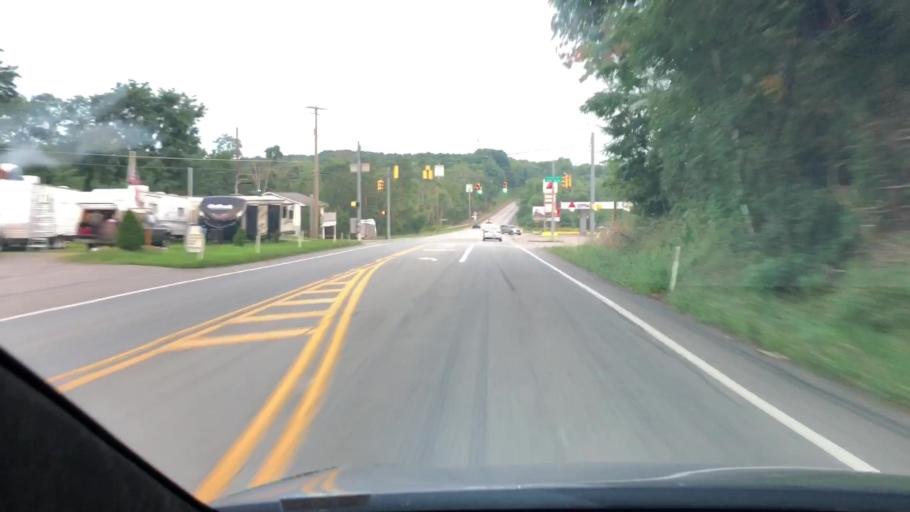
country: US
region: Pennsylvania
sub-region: Butler County
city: Slippery Rock
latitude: 40.9949
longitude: -79.9855
